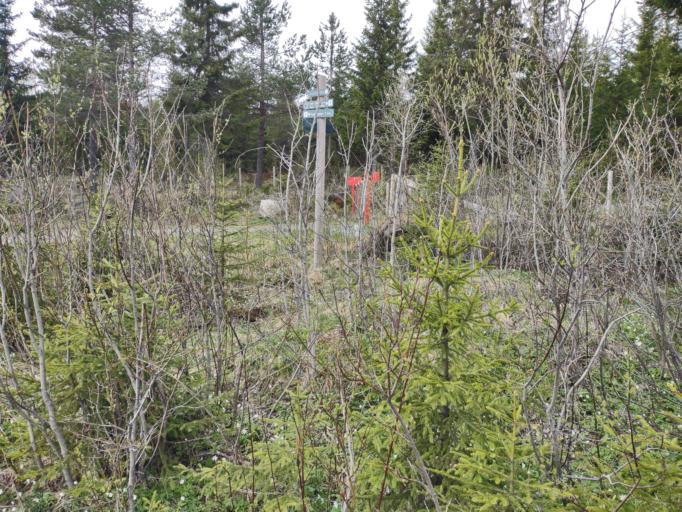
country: NO
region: Oppland
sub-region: Gran
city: Jaren
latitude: 60.4497
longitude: 10.6224
